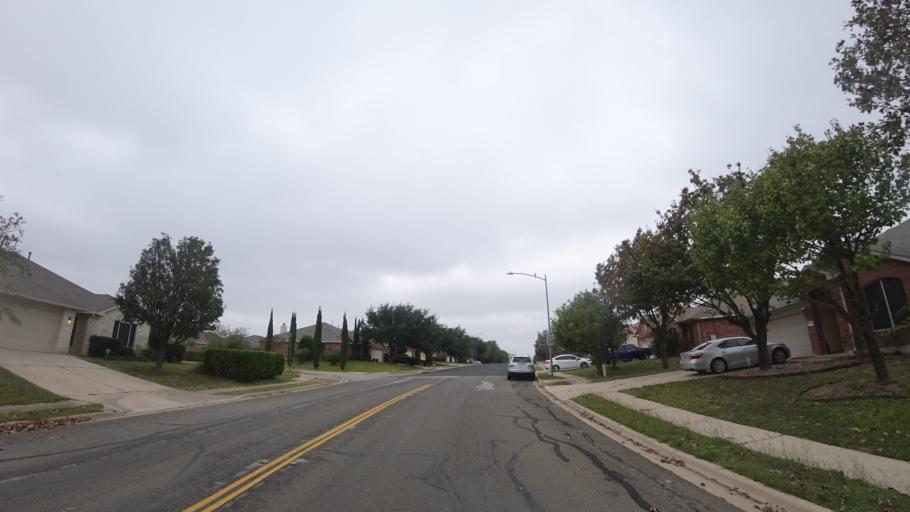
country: US
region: Texas
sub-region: Travis County
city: Pflugerville
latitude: 30.3953
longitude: -97.6465
